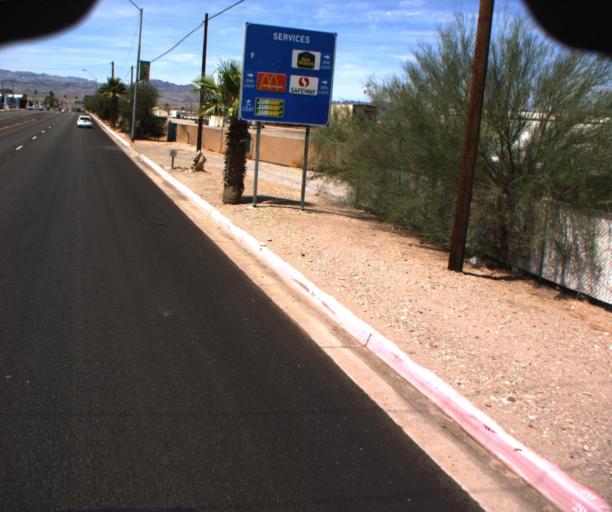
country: US
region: Arizona
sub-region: La Paz County
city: Parker
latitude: 34.1455
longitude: -114.2860
